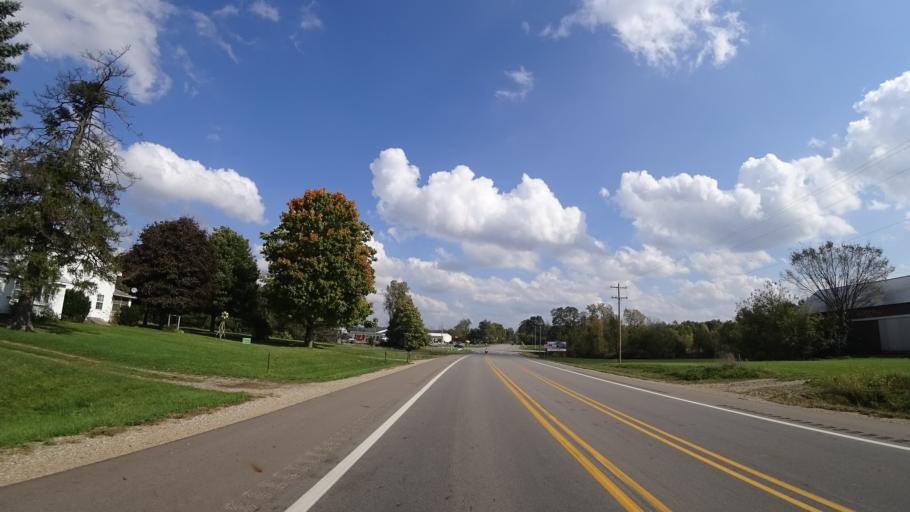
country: US
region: Michigan
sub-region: Calhoun County
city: Athens
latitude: 42.0615
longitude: -85.2370
